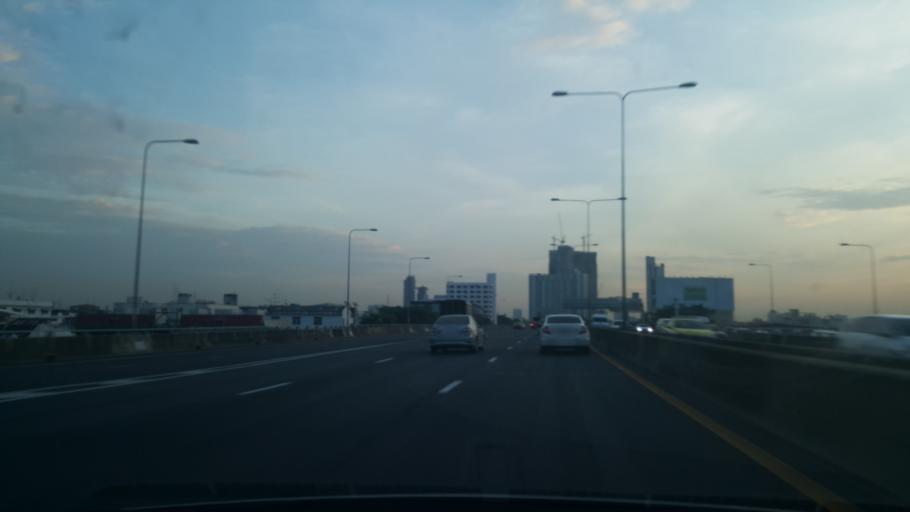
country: TH
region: Bangkok
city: Sathon
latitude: 13.7105
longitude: 100.5194
